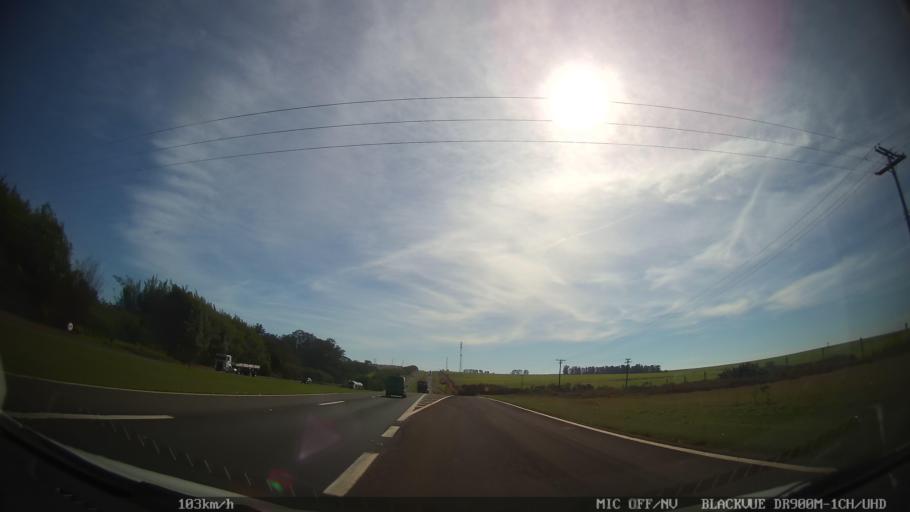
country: BR
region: Sao Paulo
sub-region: Araras
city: Araras
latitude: -22.2769
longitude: -47.3924
